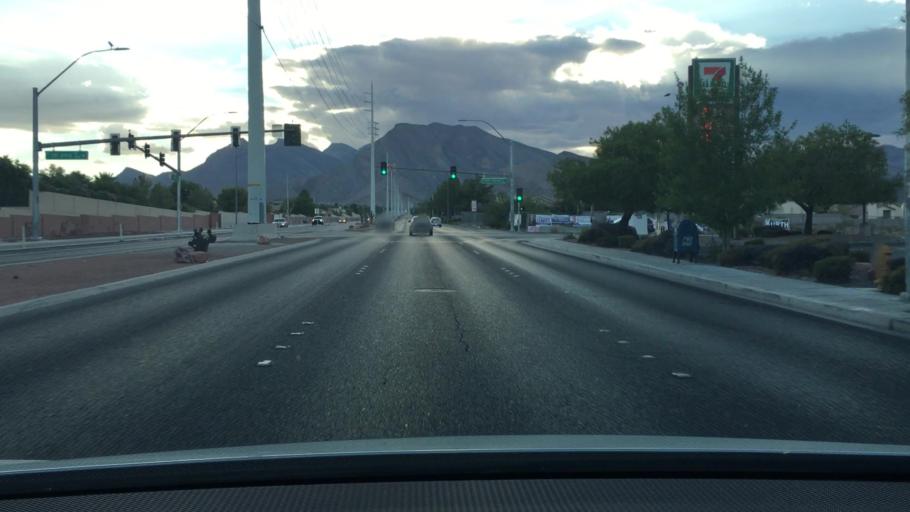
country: US
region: Nevada
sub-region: Clark County
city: Summerlin South
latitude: 36.2186
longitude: -115.2965
